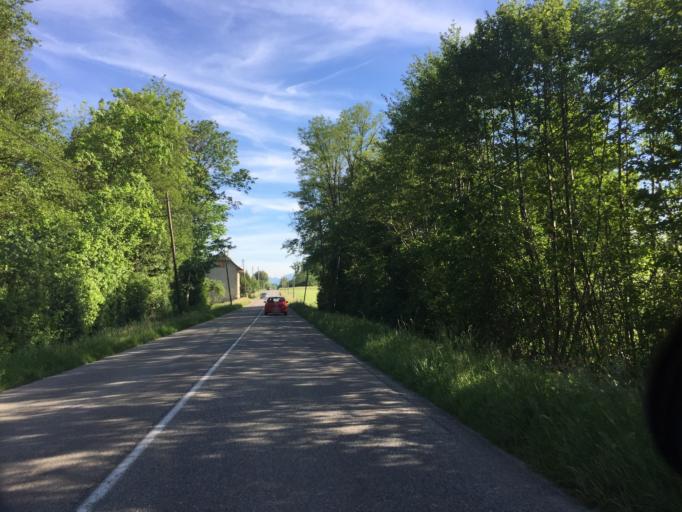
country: FR
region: Rhone-Alpes
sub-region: Departement de la Savoie
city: Albens
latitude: 45.8021
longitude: 5.9495
